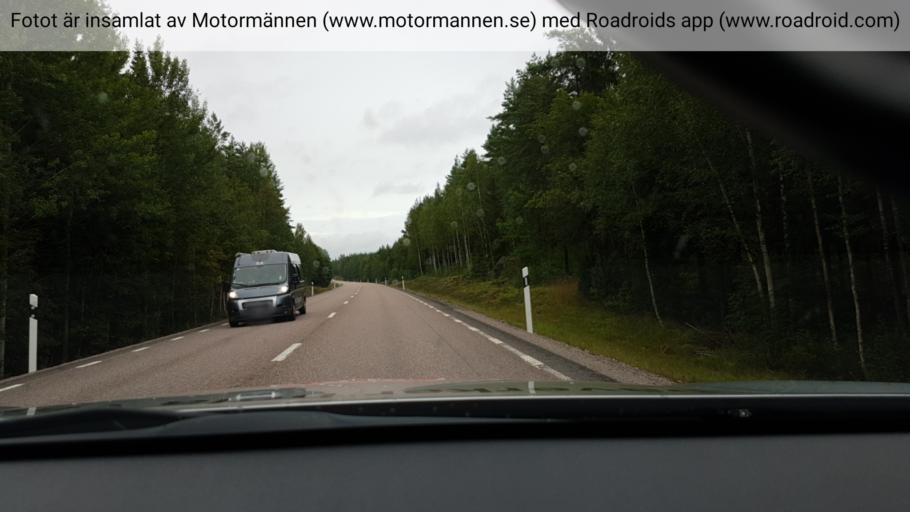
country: SE
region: Gaevleborg
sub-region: Gavle Kommun
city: Hedesunda
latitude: 60.3466
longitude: 16.9537
